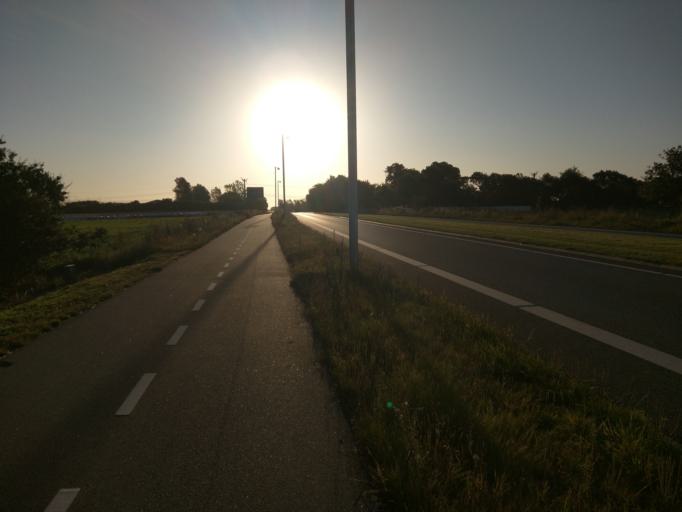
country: DK
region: Central Jutland
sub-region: Viborg Kommune
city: Bjerringbro
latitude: 56.4732
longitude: 9.5560
